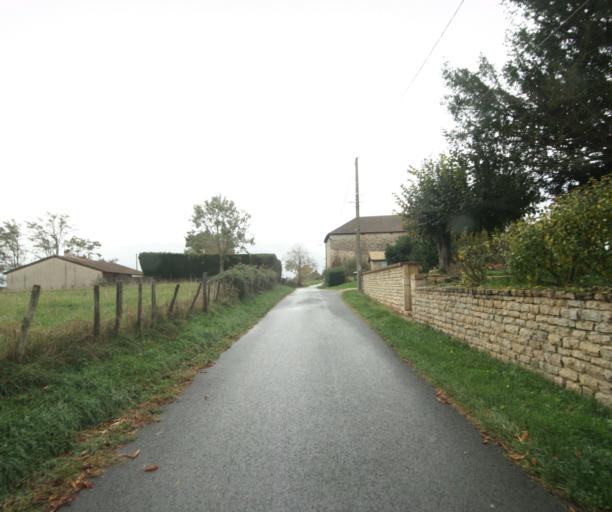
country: FR
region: Rhone-Alpes
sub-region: Departement de l'Ain
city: Pont-de-Vaux
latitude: 46.4695
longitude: 4.8858
